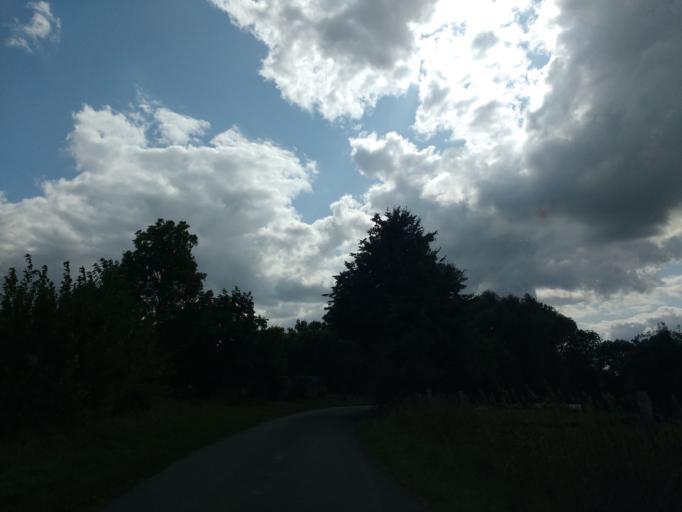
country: DE
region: North Rhine-Westphalia
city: Lichtenau
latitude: 51.6682
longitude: 8.8402
